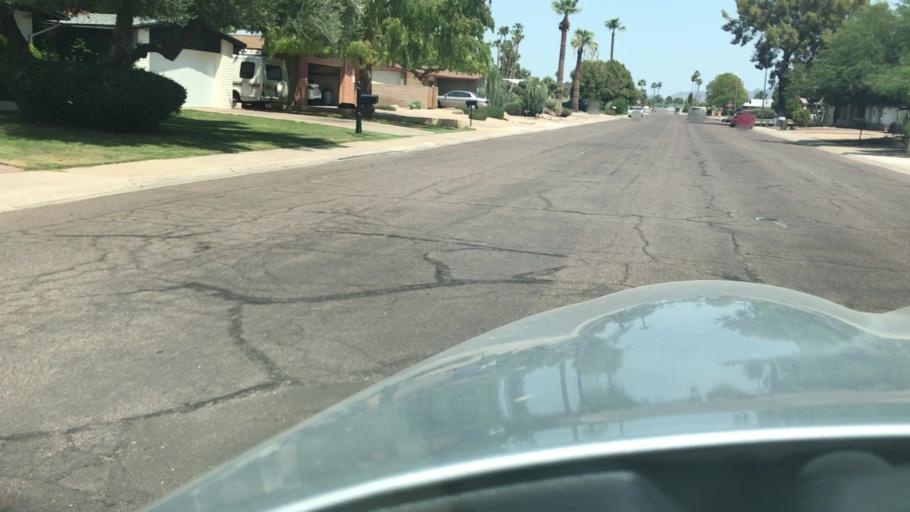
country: US
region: Arizona
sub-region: Maricopa County
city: Glendale
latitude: 33.5579
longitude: -112.1574
